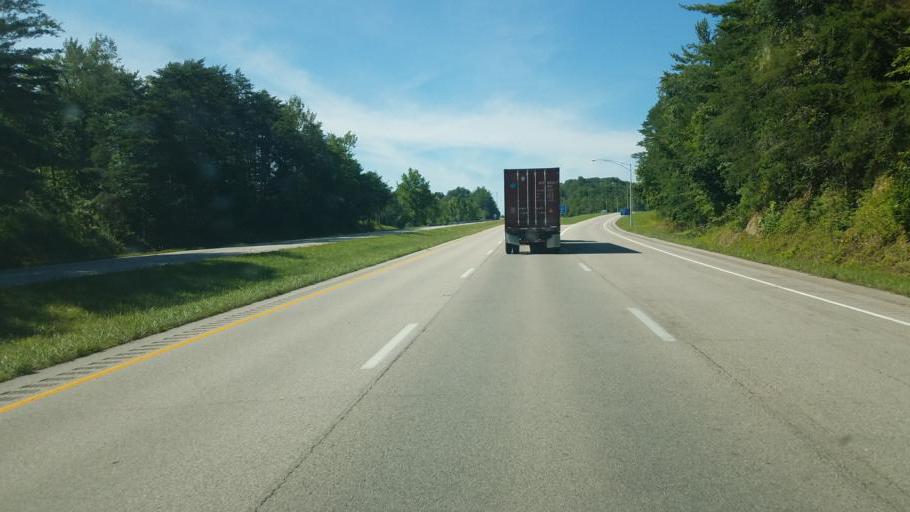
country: US
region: Ohio
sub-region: Meigs County
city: Pomeroy
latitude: 39.1151
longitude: -82.0157
